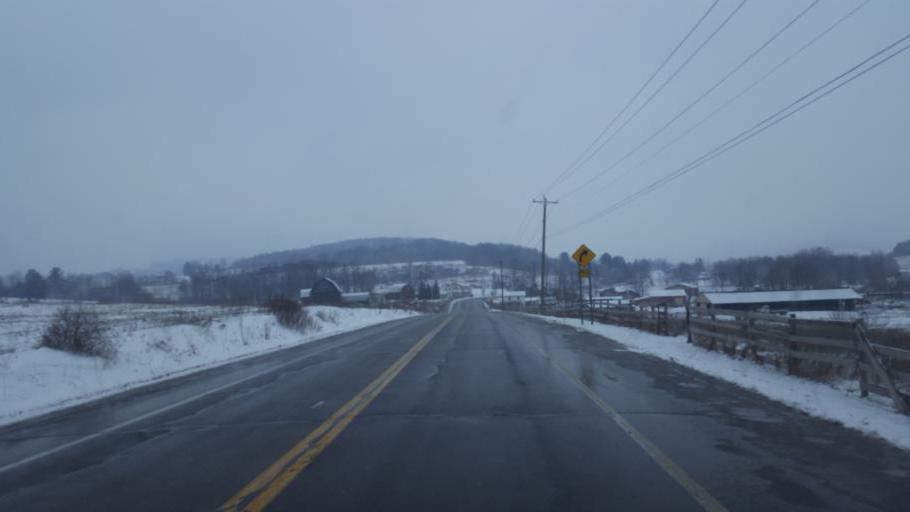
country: US
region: New York
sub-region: Steuben County
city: Canisteo
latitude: 42.1121
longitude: -77.4875
